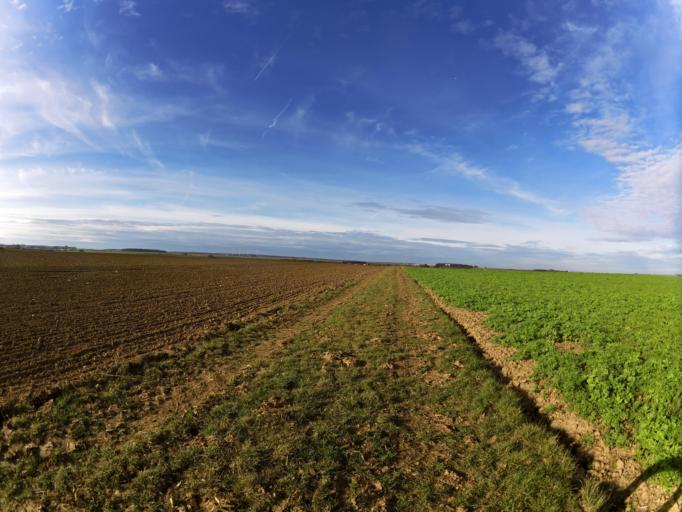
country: DE
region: Bavaria
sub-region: Regierungsbezirk Unterfranken
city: Giebelstadt
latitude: 49.6604
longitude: 9.9645
